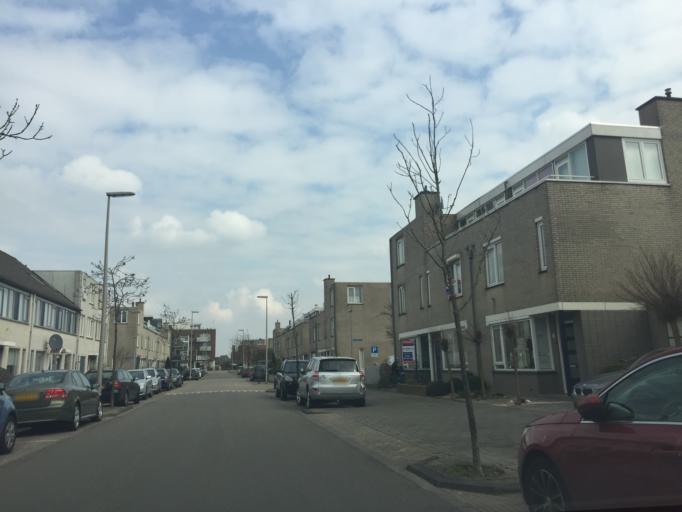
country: NL
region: South Holland
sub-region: Gemeente Alphen aan den Rijn
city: Alphen aan den Rijn
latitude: 52.1188
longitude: 4.6661
